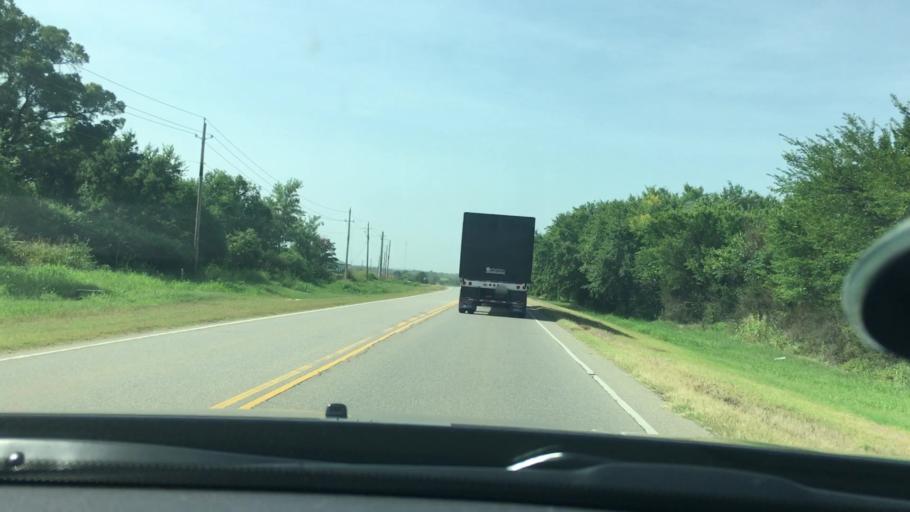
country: US
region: Oklahoma
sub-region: Coal County
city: Coalgate
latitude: 34.4670
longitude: -96.2174
